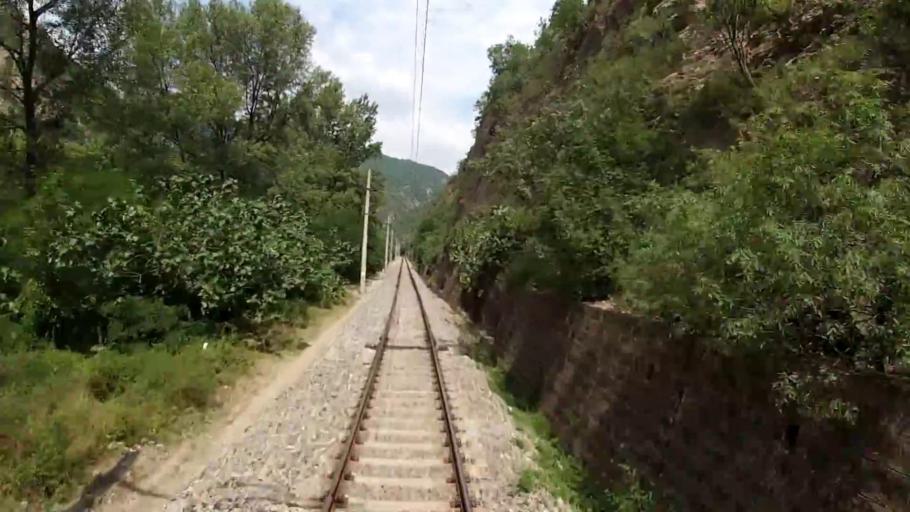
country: BG
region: Blagoevgrad
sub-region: Obshtina Kresna
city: Stara Kresna
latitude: 41.7967
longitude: 23.1593
